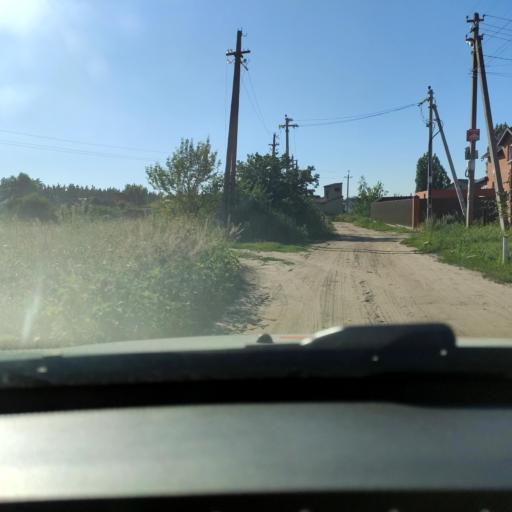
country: RU
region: Voronezj
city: Pridonskoy
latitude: 51.6306
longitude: 39.0898
